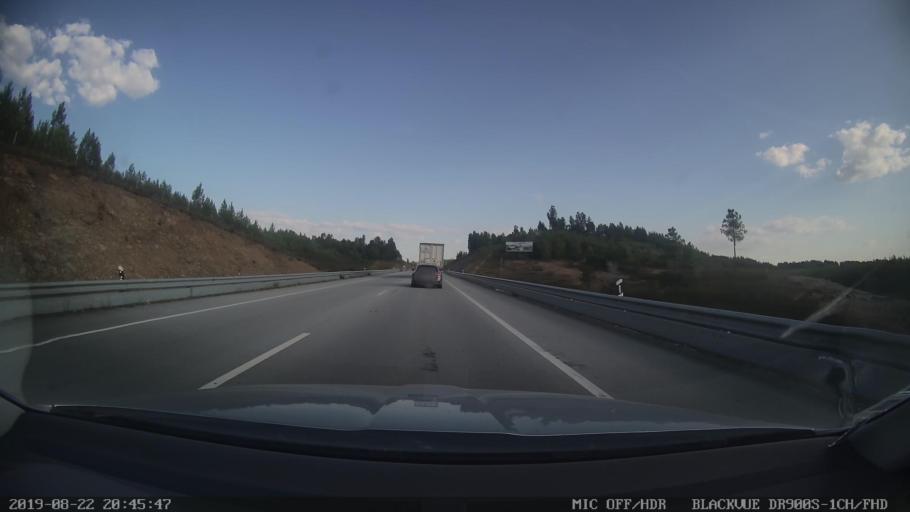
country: PT
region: Castelo Branco
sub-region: Proenca-A-Nova
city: Proenca-a-Nova
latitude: 39.7204
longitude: -7.8700
